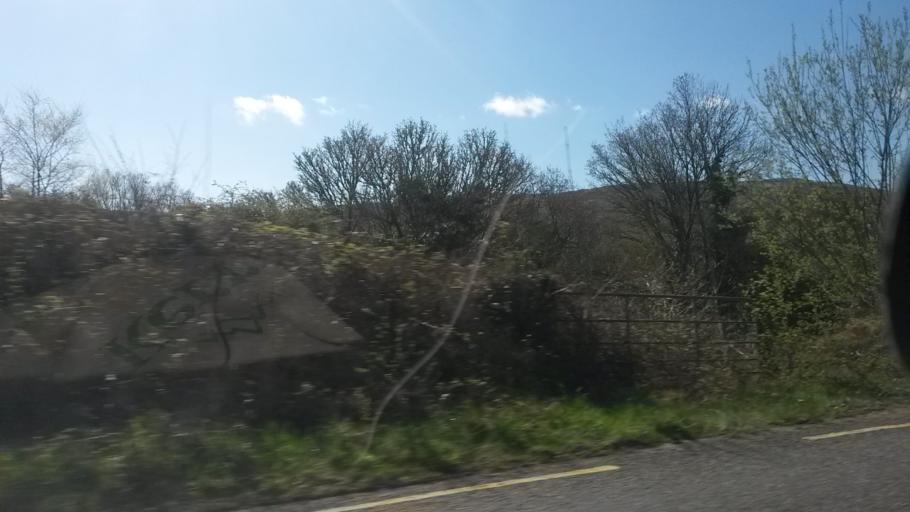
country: IE
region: Munster
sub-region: Ciarrai
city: Cill Airne
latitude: 51.9200
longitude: -9.3890
